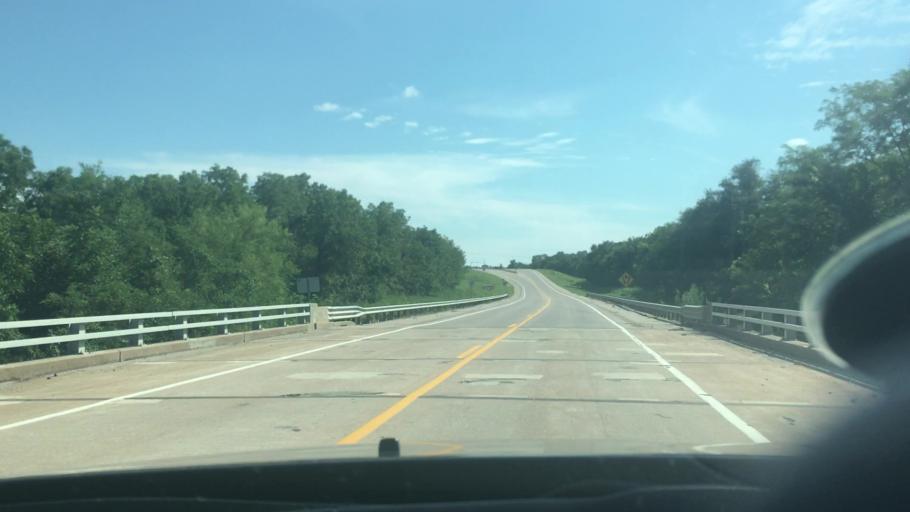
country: US
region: Oklahoma
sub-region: Seminole County
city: Konawa
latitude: 34.9481
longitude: -96.6807
